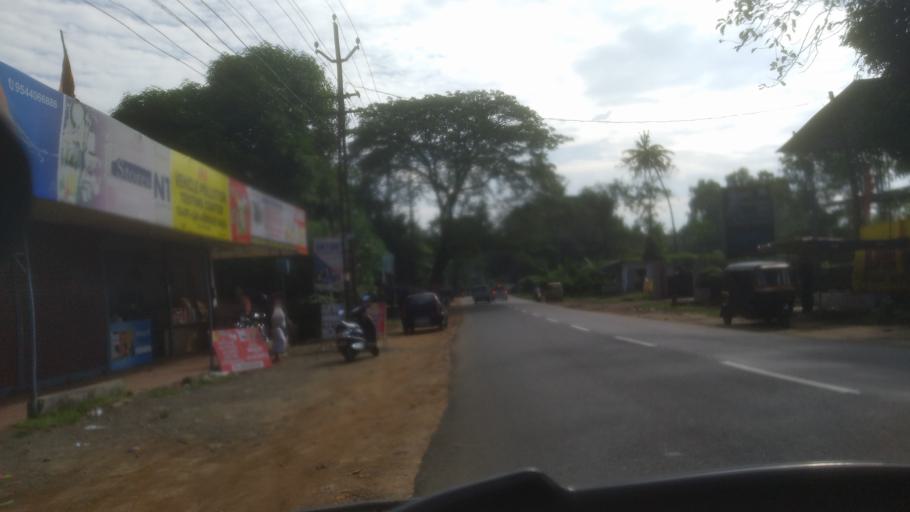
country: IN
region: Kerala
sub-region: Ernakulam
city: Kotamangalam
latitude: 10.0588
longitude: 76.6780
